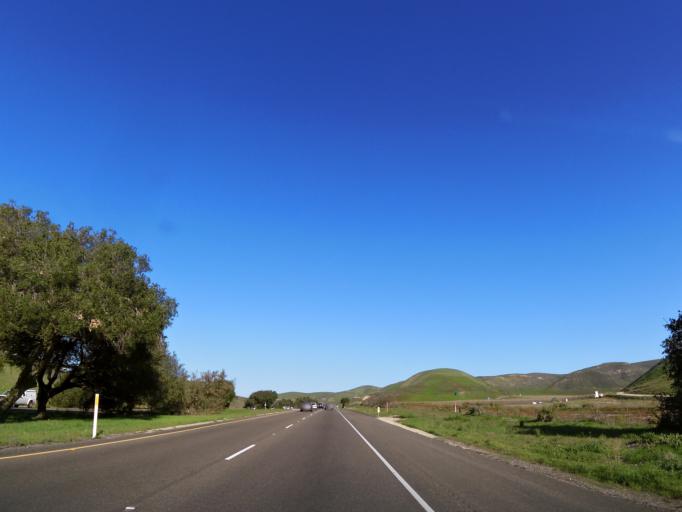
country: US
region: California
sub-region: Santa Barbara County
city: Los Alamos
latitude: 34.8025
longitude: -120.3424
